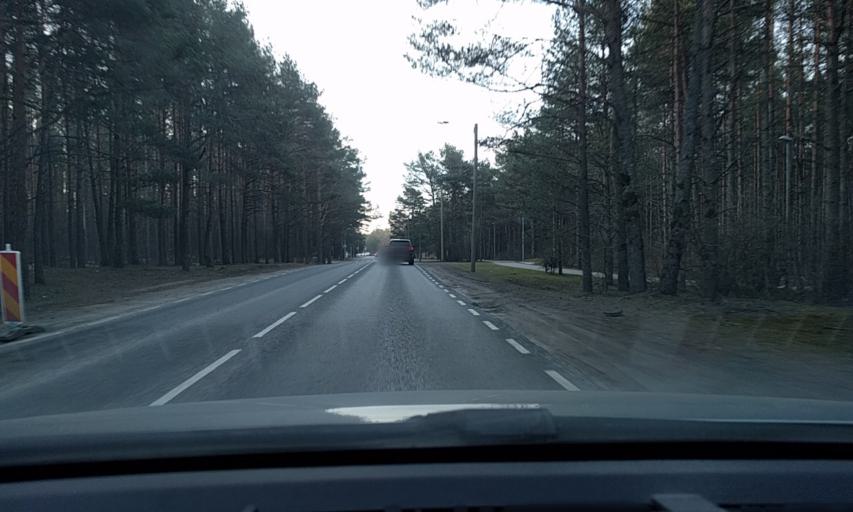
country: EE
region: Harju
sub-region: Tallinna linn
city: Kose
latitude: 59.4756
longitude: 24.8954
